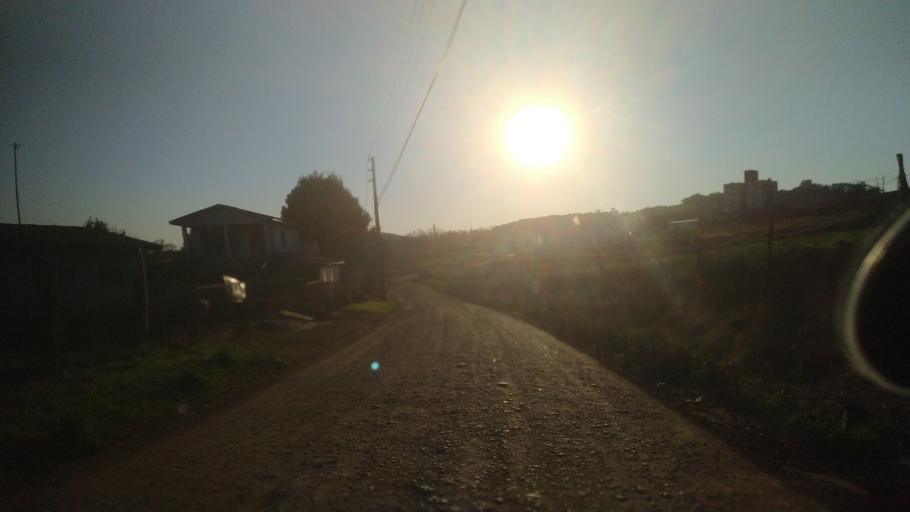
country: BR
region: Santa Catarina
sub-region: Chapeco
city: Chapeco
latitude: -27.0373
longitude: -52.6294
